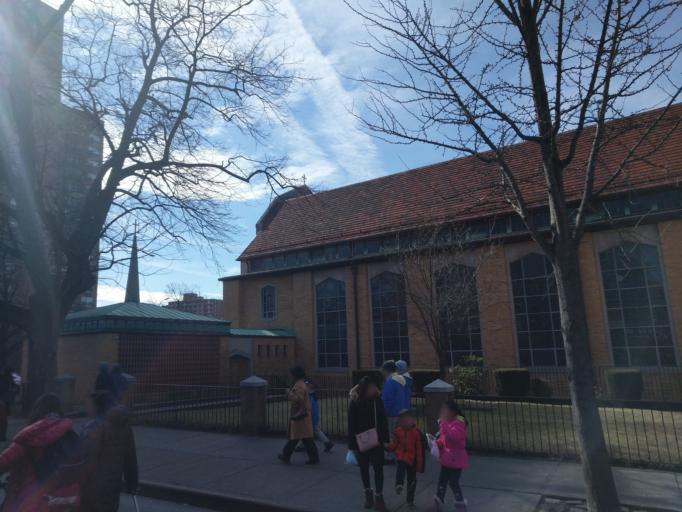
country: US
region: New York
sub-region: Queens County
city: Jamaica
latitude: 40.7590
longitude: -73.8258
